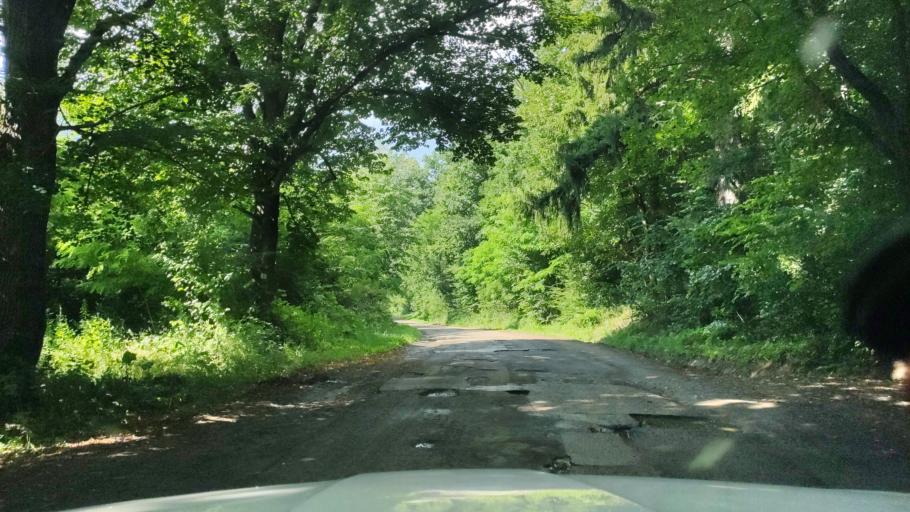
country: HU
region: Heves
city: Parad
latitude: 47.9152
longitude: 20.0587
